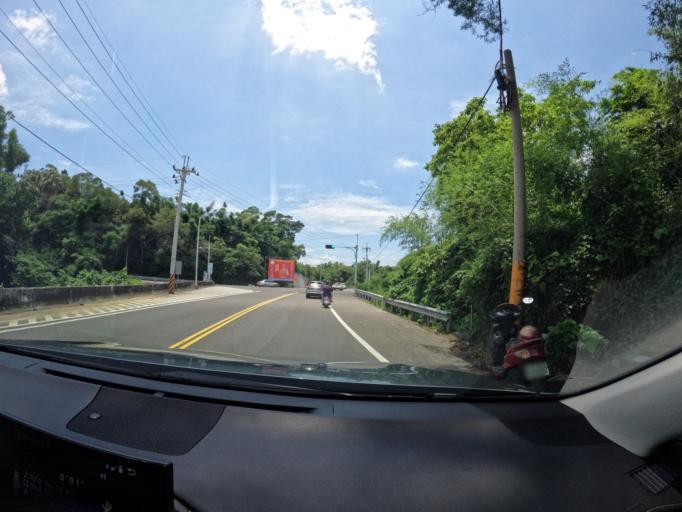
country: TW
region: Taiwan
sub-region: Hsinchu
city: Hsinchu
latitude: 24.6725
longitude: 120.9530
